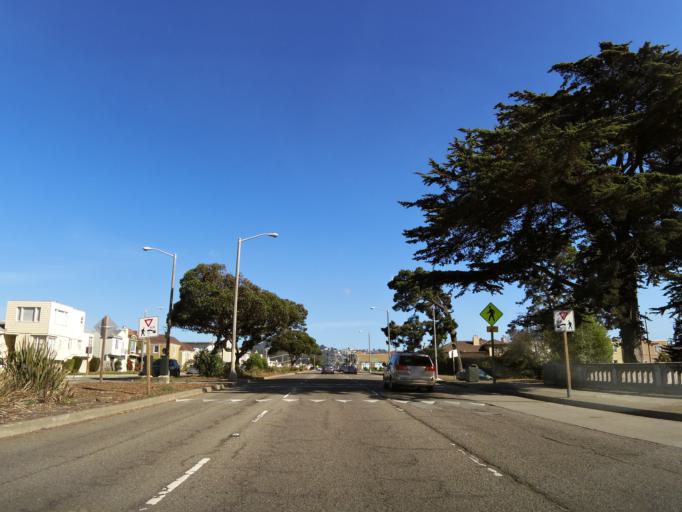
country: US
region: California
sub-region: San Mateo County
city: Daly City
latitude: 37.7339
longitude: -122.4938
